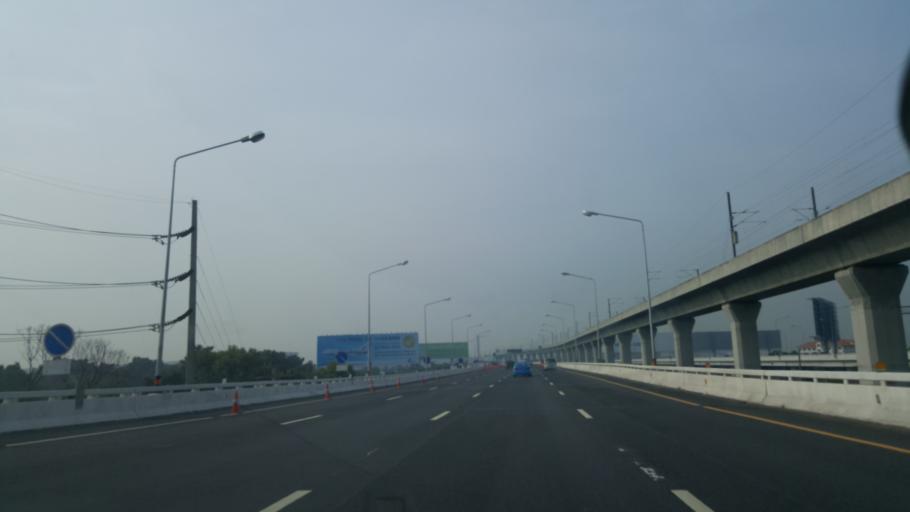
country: TH
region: Bangkok
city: Lat Krabang
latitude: 13.7227
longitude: 100.7599
